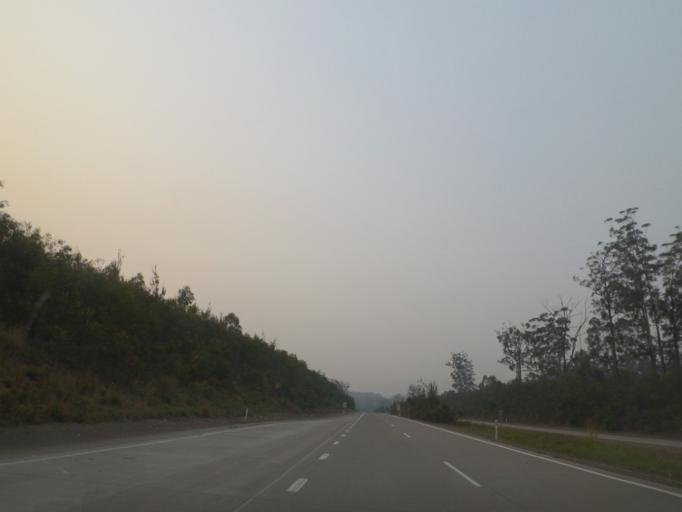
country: AU
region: New South Wales
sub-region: Nambucca Shire
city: Macksville
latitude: -30.8753
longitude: 152.9319
